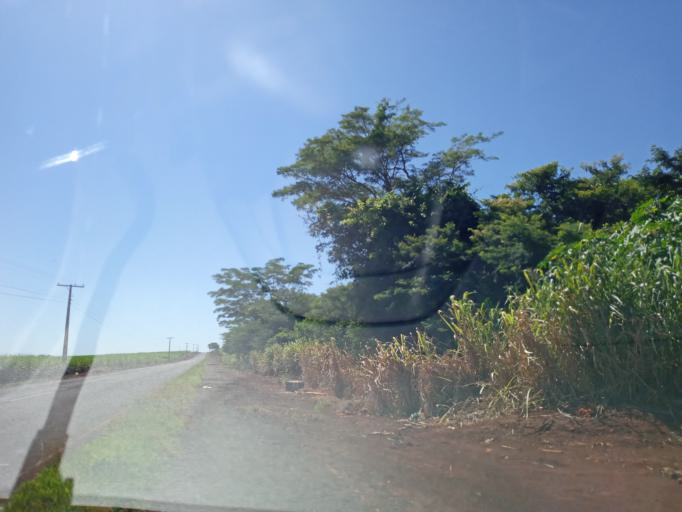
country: BR
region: Goias
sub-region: Itumbiara
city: Itumbiara
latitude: -18.4257
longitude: -49.1738
